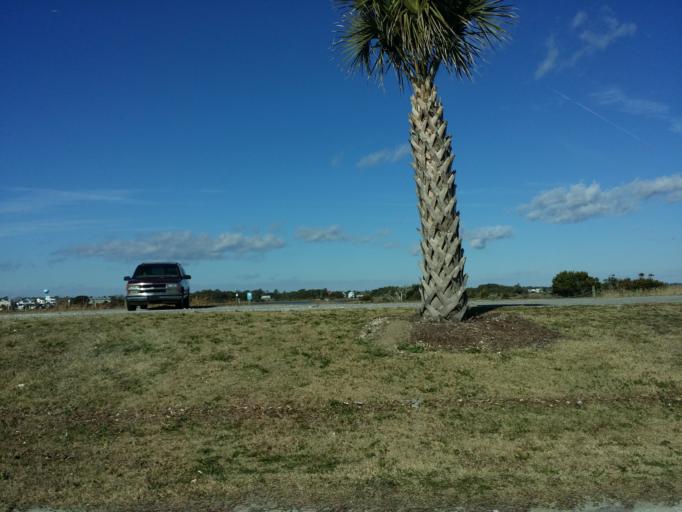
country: US
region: North Carolina
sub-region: Pender County
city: Surf City
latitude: 34.4286
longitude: -77.5433
